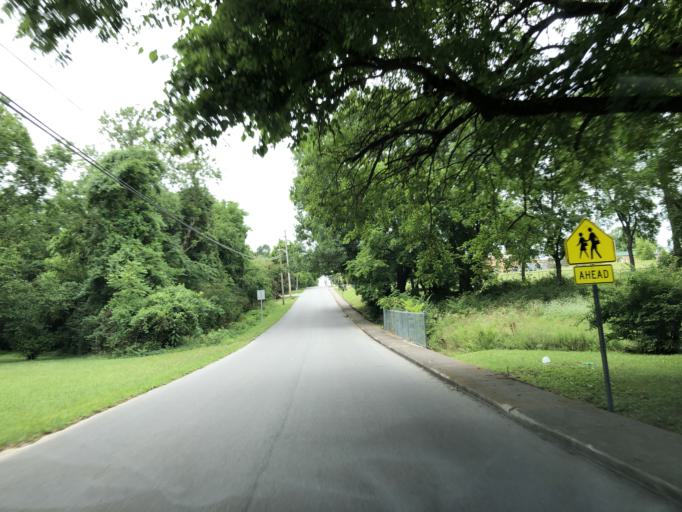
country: US
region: Tennessee
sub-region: Davidson County
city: Goodlettsville
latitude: 36.2939
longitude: -86.7101
